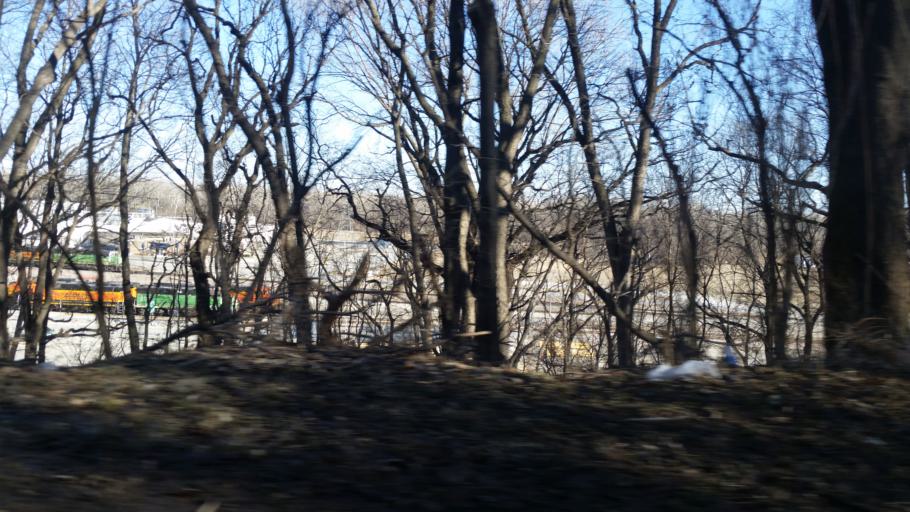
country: US
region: Nebraska
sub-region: Douglas County
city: Omaha
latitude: 41.2179
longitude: -95.9304
